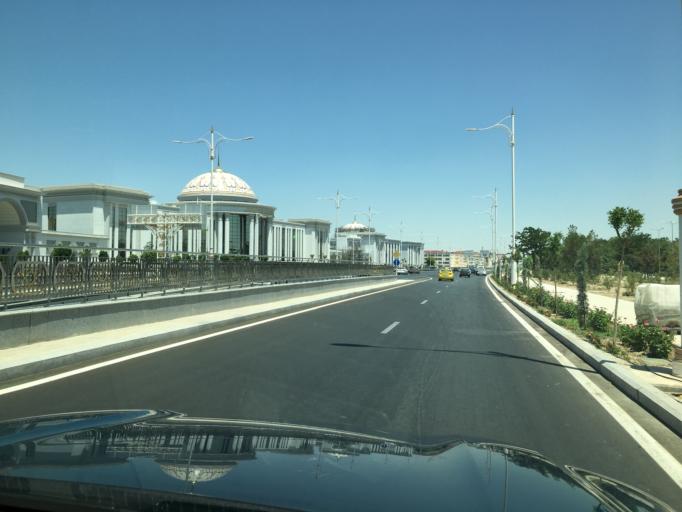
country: TM
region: Ahal
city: Ashgabat
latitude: 37.9293
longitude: 58.3924
